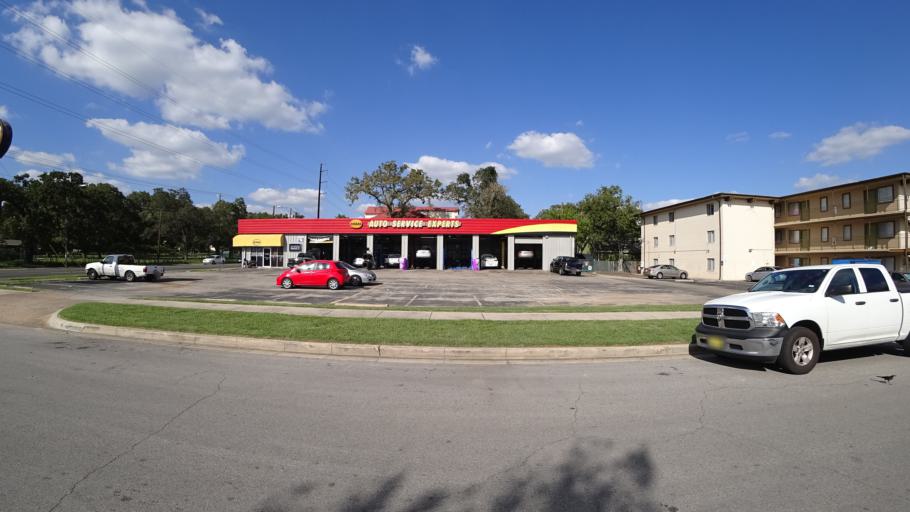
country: US
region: Texas
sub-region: Travis County
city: Austin
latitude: 30.3051
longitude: -97.7362
